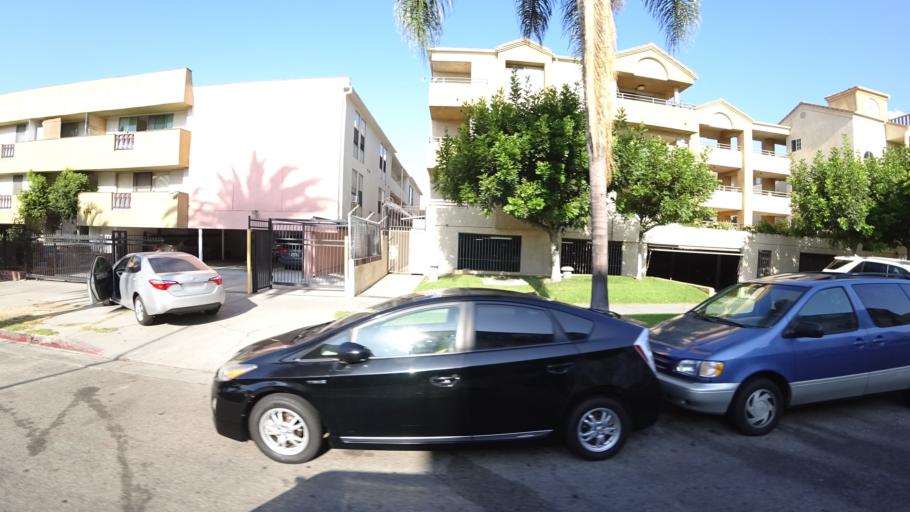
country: US
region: California
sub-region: Los Angeles County
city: Hollywood
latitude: 34.0589
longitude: -118.3079
